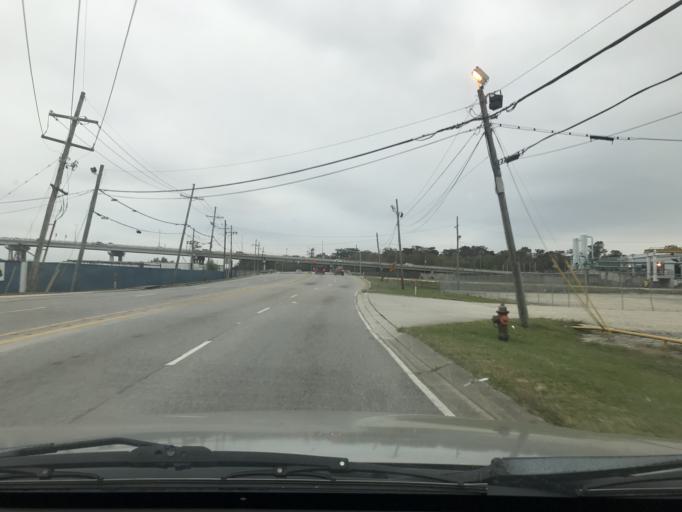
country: US
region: Louisiana
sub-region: Jefferson Parish
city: Woodmere
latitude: 29.8729
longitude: -90.0728
